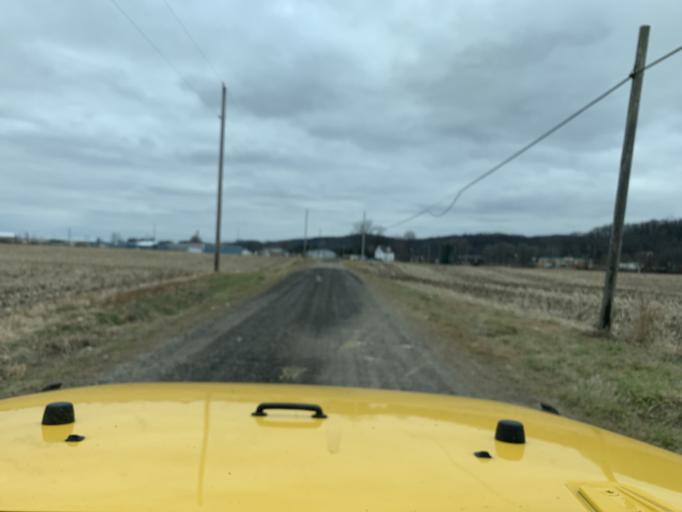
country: US
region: Ohio
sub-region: Tuscarawas County
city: Newcomerstown
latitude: 40.2832
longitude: -81.5619
